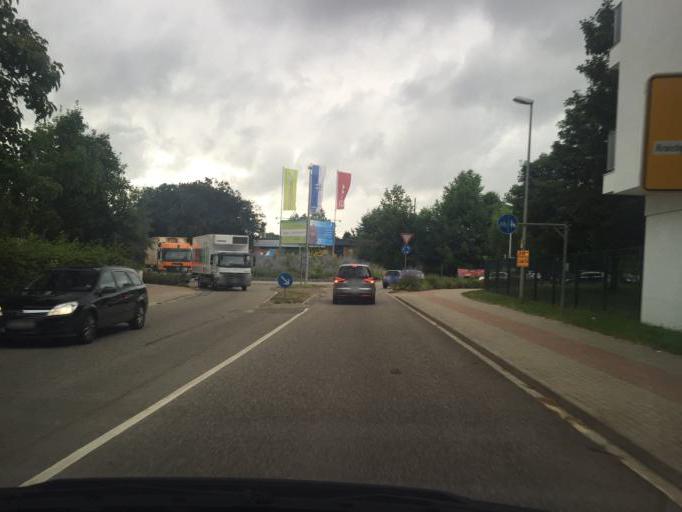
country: DE
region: Baden-Wuerttemberg
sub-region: Karlsruhe Region
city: Bretten
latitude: 49.0310
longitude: 8.7053
